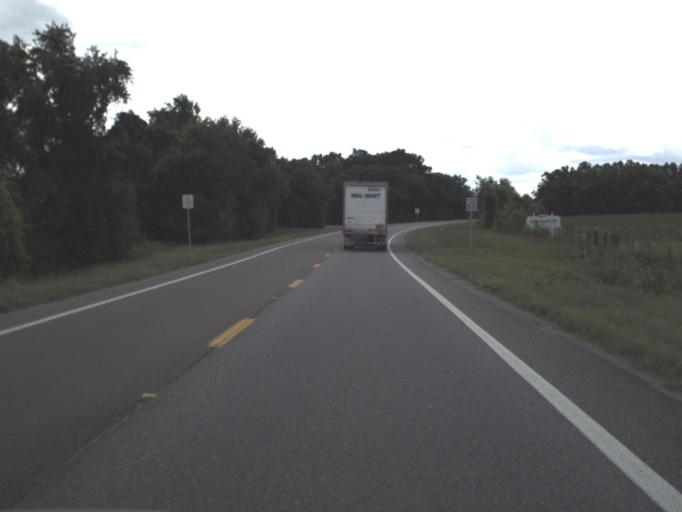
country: US
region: Florida
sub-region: Alachua County
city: Newberry
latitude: 29.6347
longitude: -82.6060
